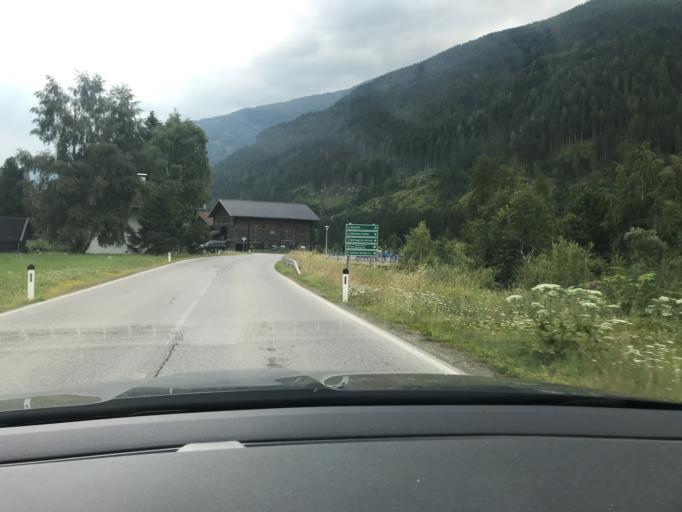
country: AT
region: Tyrol
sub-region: Politischer Bezirk Lienz
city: Innervillgraten
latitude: 46.9157
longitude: 12.3752
